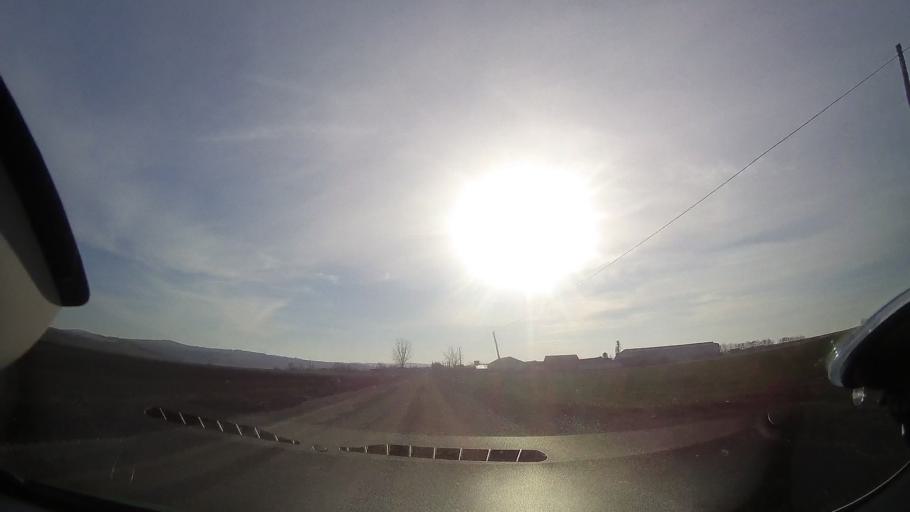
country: RO
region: Bihor
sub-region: Comuna Sarbi
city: Sarbi
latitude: 47.2144
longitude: 22.1330
